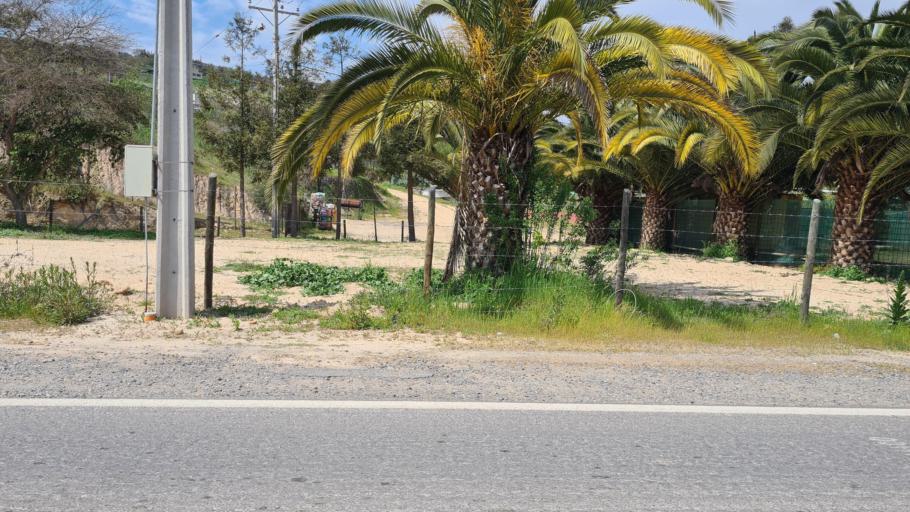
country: CL
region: O'Higgins
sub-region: Provincia de Cachapoal
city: San Vicente
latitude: -34.1569
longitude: -71.4245
